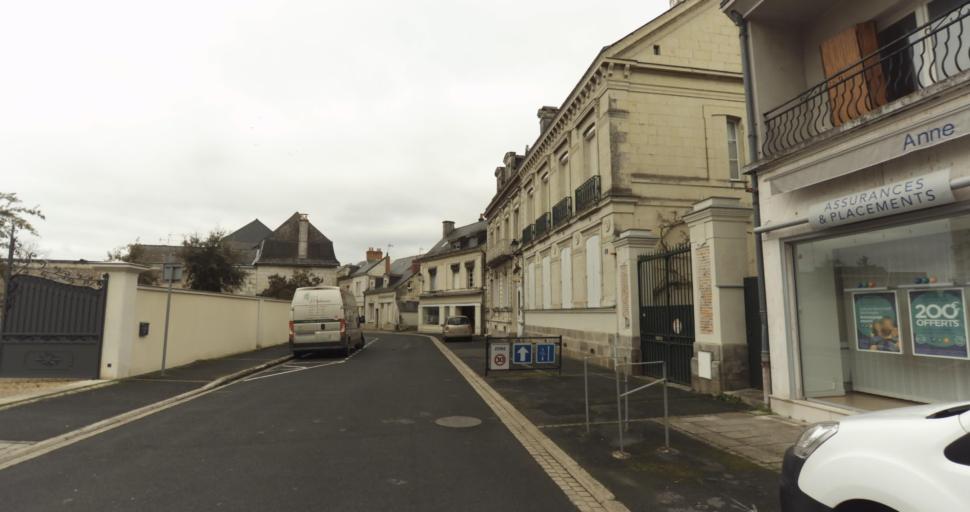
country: FR
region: Pays de la Loire
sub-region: Departement de Maine-et-Loire
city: Jumelles
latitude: 47.3814
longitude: -0.1106
